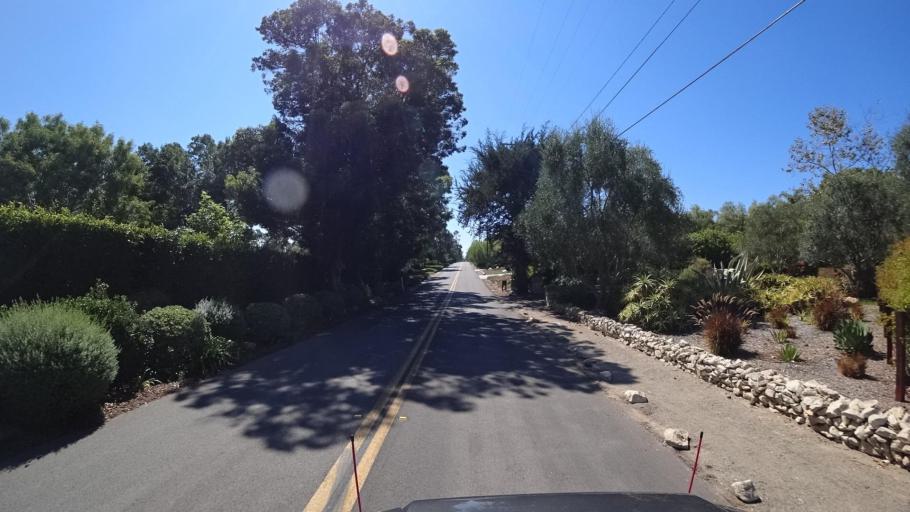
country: US
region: California
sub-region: San Diego County
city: Rancho Santa Fe
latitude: 33.0334
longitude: -117.1966
